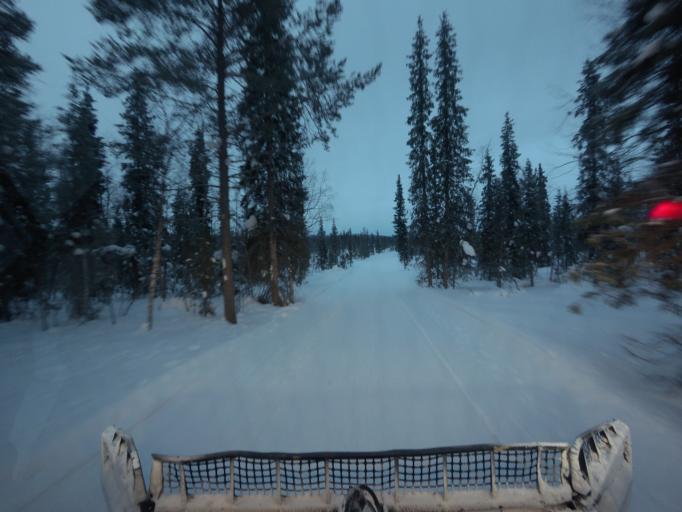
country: FI
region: Lapland
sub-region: Tunturi-Lappi
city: Kolari
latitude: 67.6168
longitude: 24.1675
